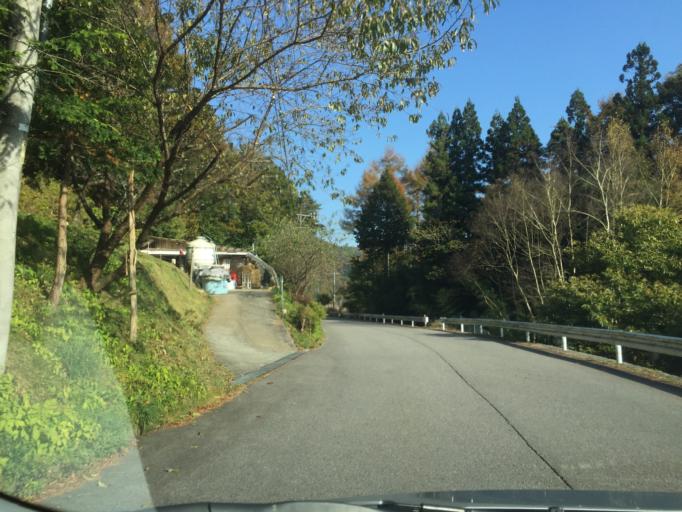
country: JP
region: Nagano
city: Iida
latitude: 35.3740
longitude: 137.6815
